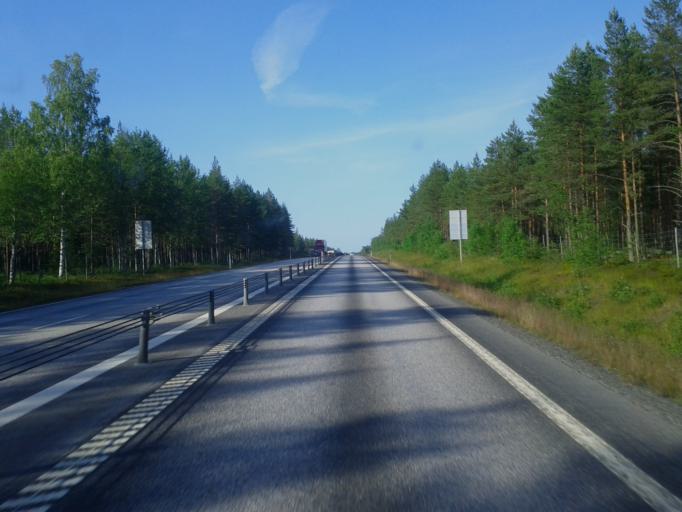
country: SE
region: Vaesterbotten
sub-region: Umea Kommun
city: Saevar
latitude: 63.9376
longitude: 20.6474
